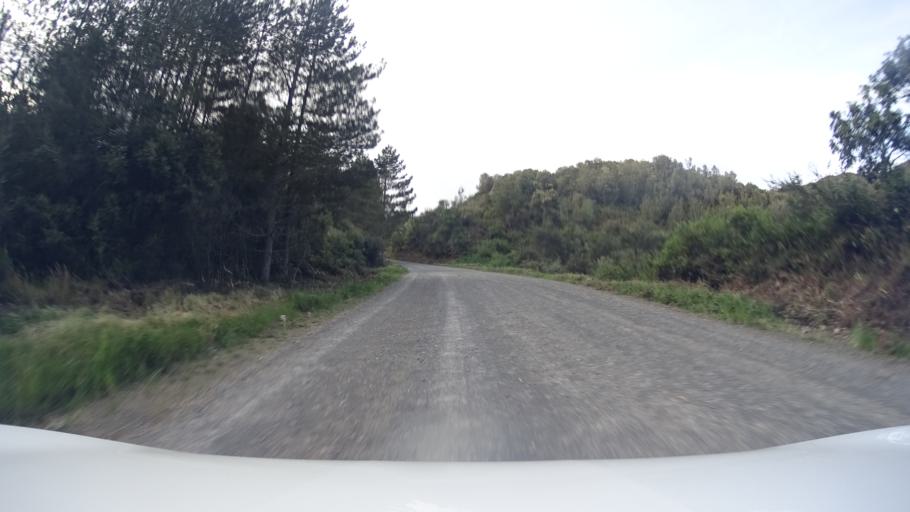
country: NZ
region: Bay of Plenty
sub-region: Rotorua District
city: Rotorua
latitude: -38.3270
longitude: 176.3750
